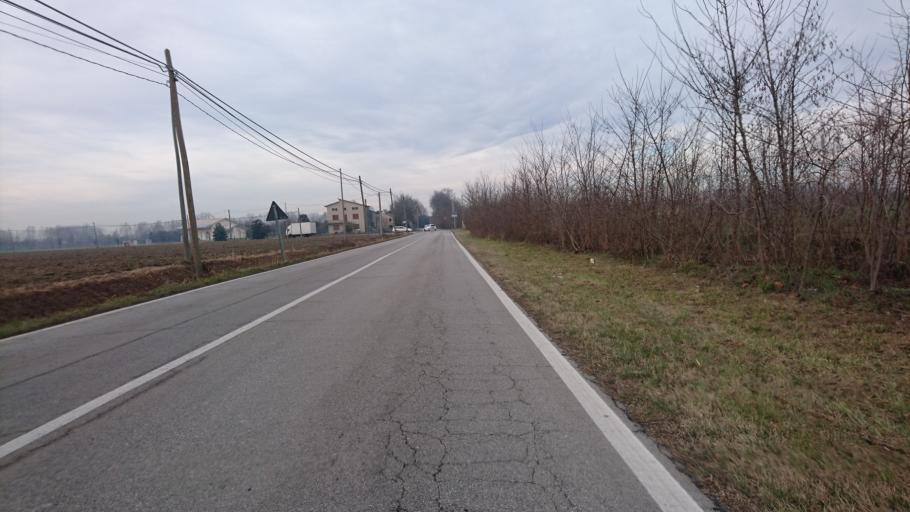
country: IT
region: Veneto
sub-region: Provincia di Padova
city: Ronchi di Campanile
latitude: 45.4677
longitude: 11.7938
